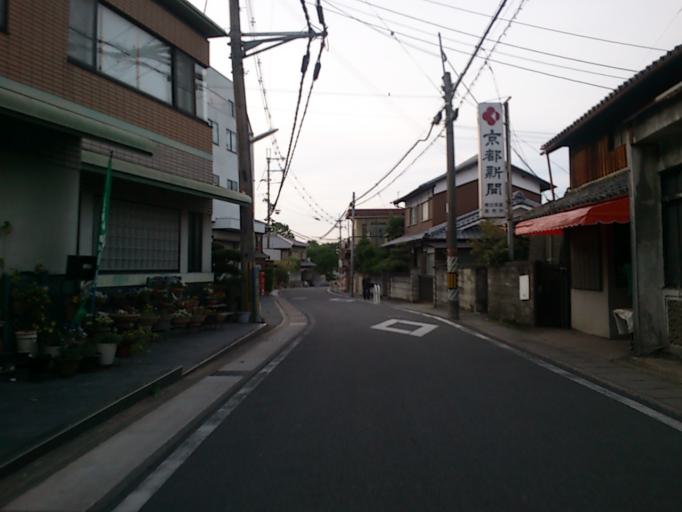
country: JP
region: Kyoto
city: Tanabe
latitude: 34.8200
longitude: 135.8071
